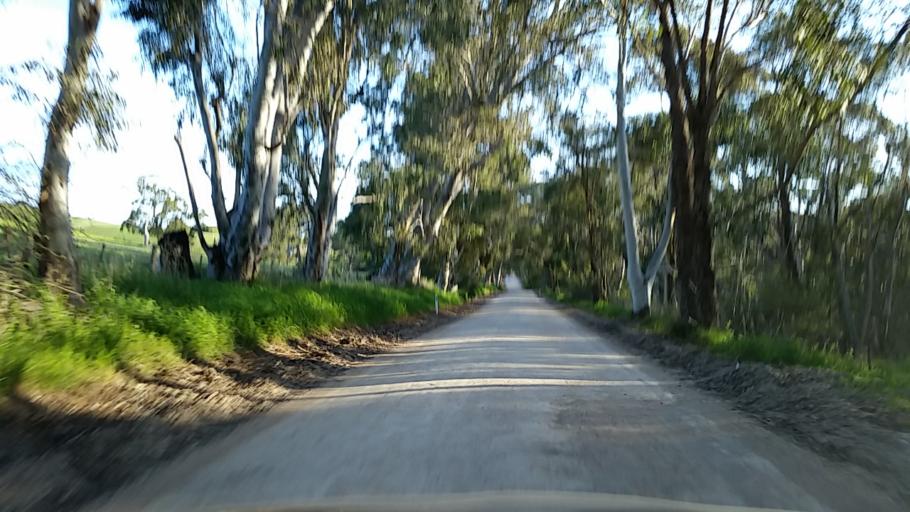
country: AU
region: South Australia
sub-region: Alexandrina
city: Mount Compass
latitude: -35.2776
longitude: 138.7007
